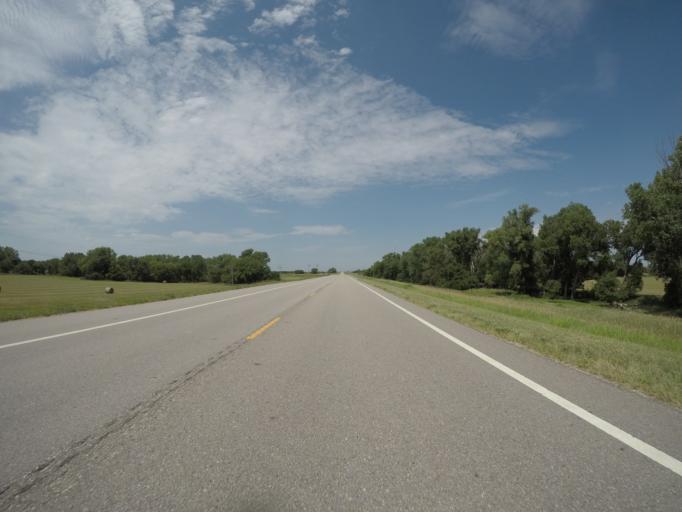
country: US
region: Kansas
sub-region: Rooks County
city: Stockton
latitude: 39.4443
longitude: -99.1900
